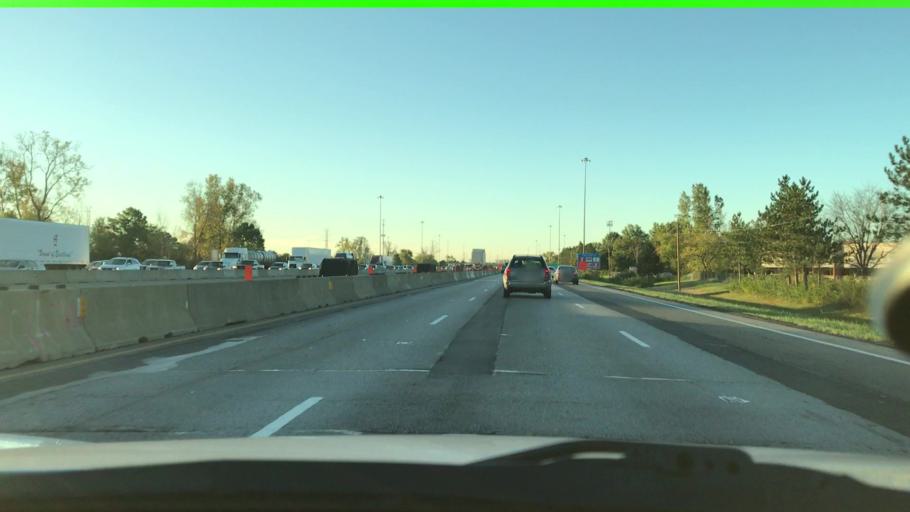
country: US
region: Ohio
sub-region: Franklin County
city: Hilliard
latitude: 40.0426
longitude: -83.1266
